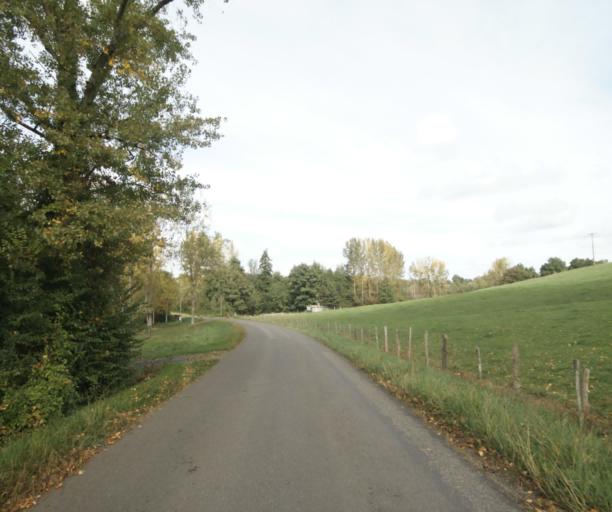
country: FR
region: Midi-Pyrenees
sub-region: Departement du Gers
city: Eauze
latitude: 43.8413
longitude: 0.1119
